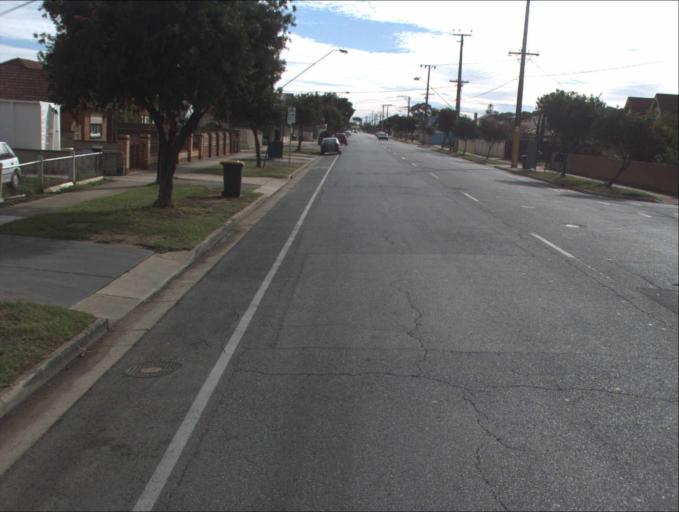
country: AU
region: South Australia
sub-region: Port Adelaide Enfield
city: Alberton
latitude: -34.8606
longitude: 138.5292
